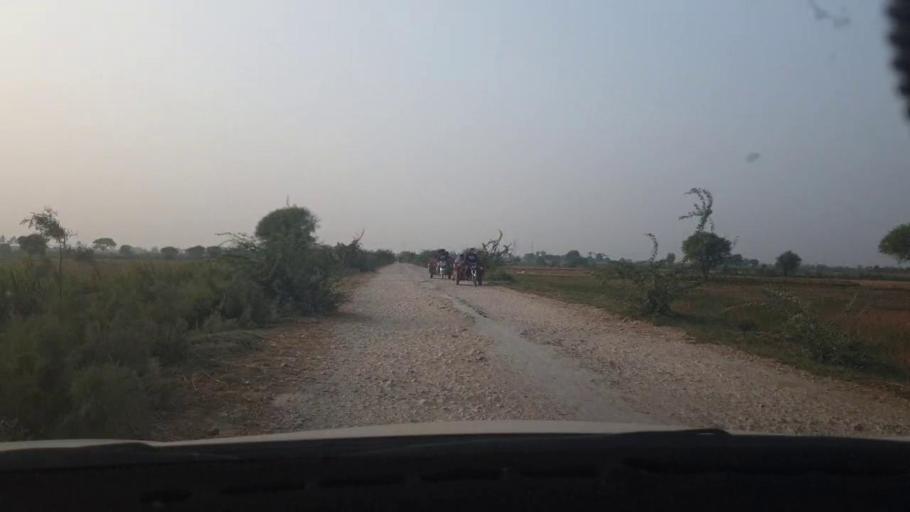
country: PK
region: Sindh
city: Bulri
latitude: 24.8508
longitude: 68.3438
